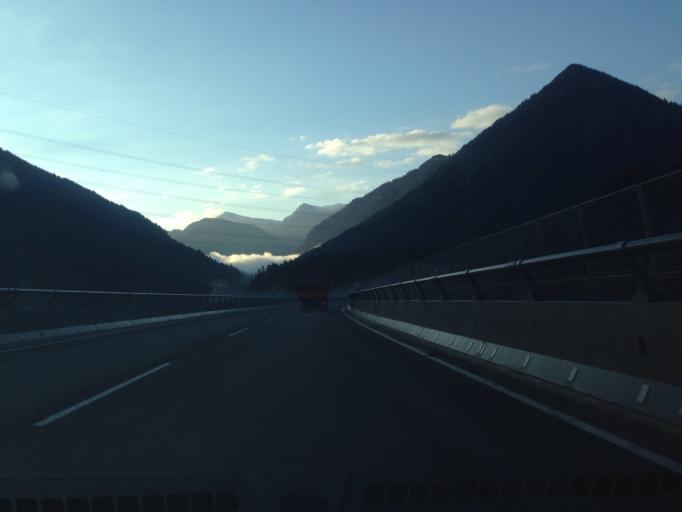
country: AT
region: Tyrol
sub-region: Politischer Bezirk Reutte
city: Breitenwang
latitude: 47.4962
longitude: 10.7441
